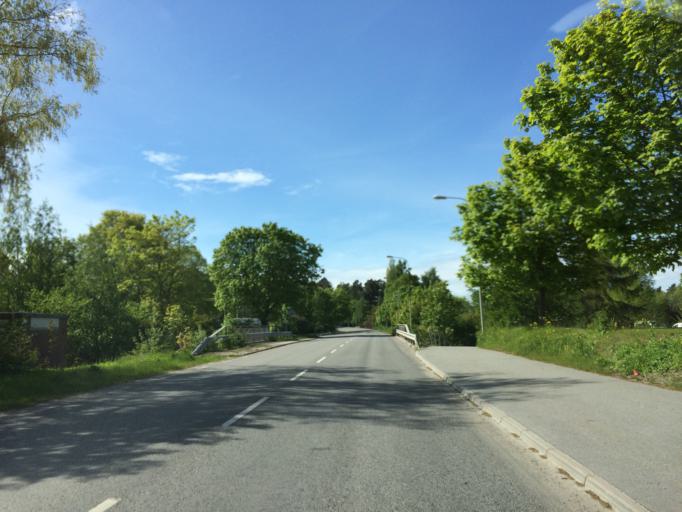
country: SE
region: Stockholm
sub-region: Sollentuna Kommun
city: Sollentuna
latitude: 59.4486
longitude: 17.9391
